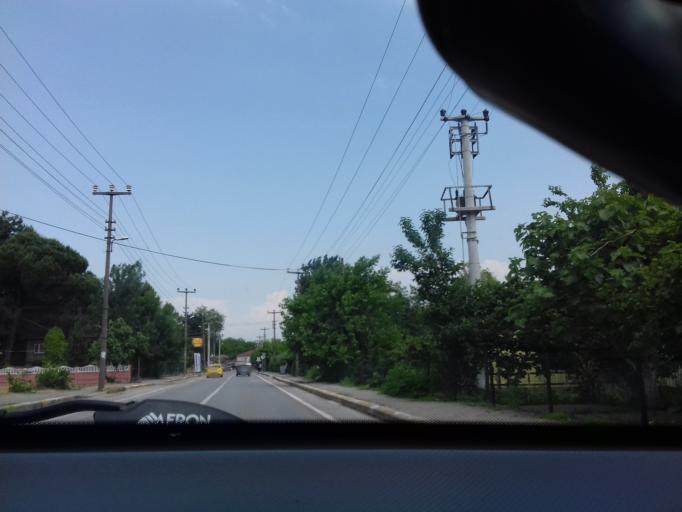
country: TR
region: Sakarya
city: Adapazari
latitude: 40.7135
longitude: 30.3585
